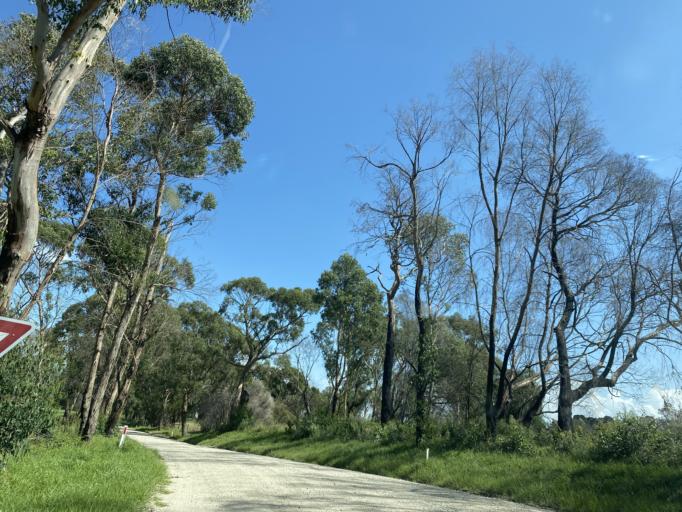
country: AU
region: Victoria
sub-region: Cardinia
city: Garfield
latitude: -38.0428
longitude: 145.6766
